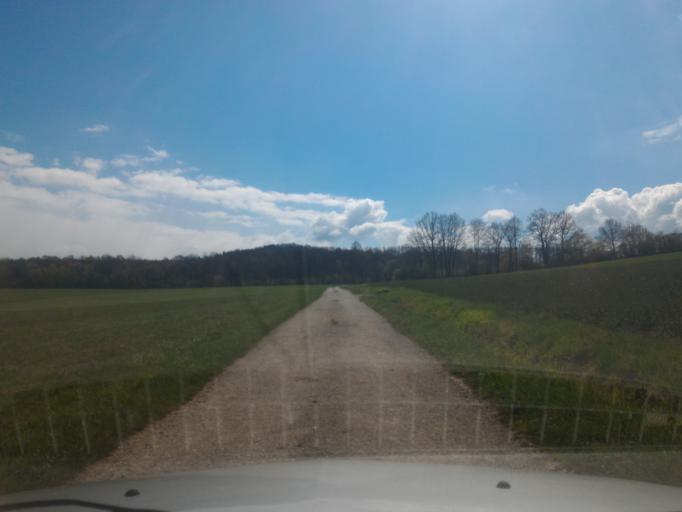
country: DE
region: Saxony
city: Leutersdorf
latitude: 50.9404
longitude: 14.6416
